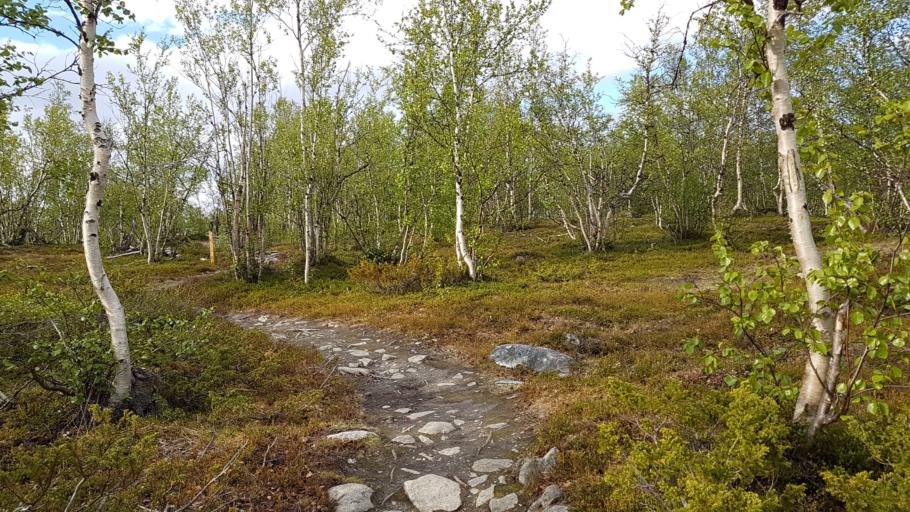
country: NO
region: Troms
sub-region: Bardu
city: Setermoen
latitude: 68.3477
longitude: 18.7805
